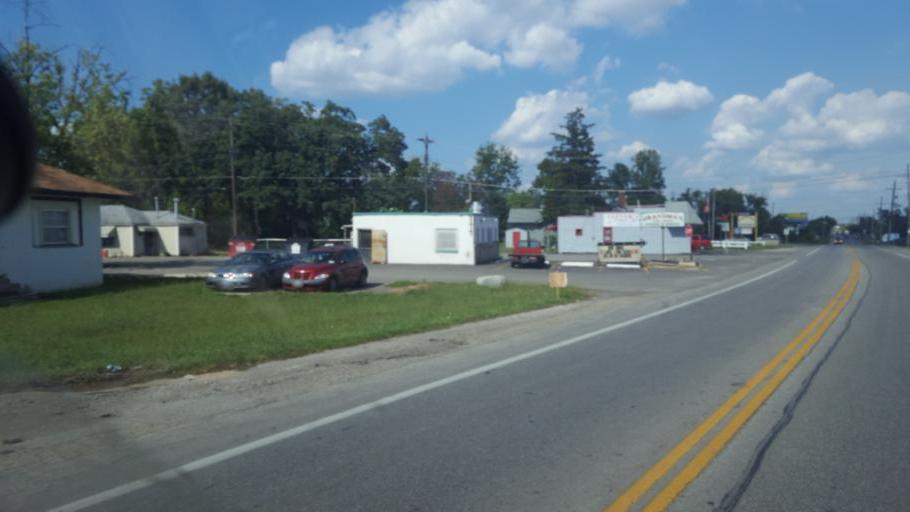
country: US
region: Ohio
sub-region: Franklin County
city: Grandview Heights
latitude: 39.9361
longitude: -83.0432
